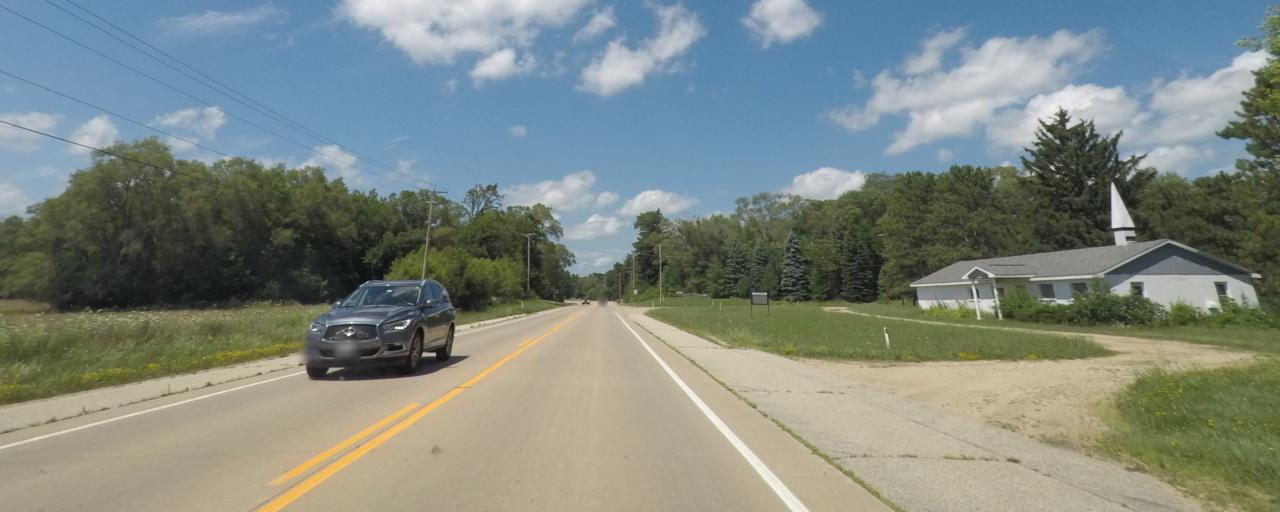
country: US
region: Wisconsin
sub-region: Jefferson County
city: Cambridge
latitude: 42.9960
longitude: -89.0010
